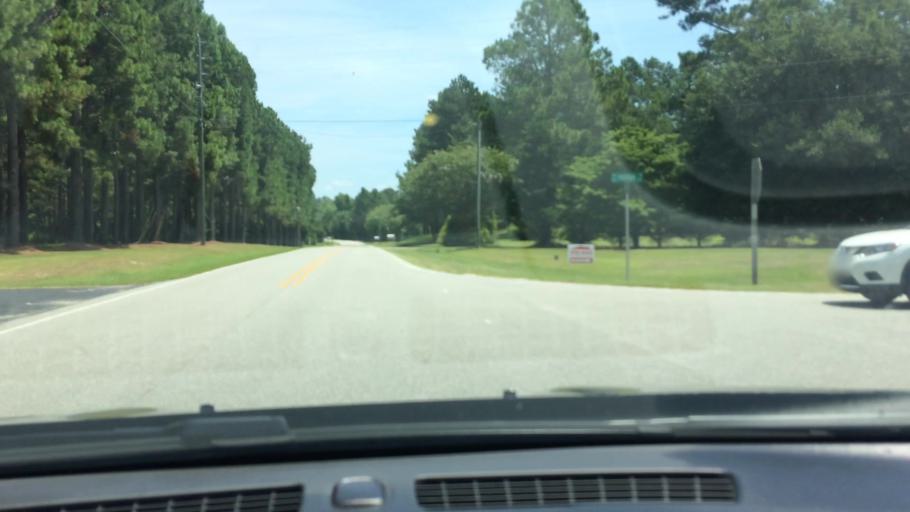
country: US
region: North Carolina
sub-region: Pitt County
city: Windsor
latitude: 35.5593
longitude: -77.2359
